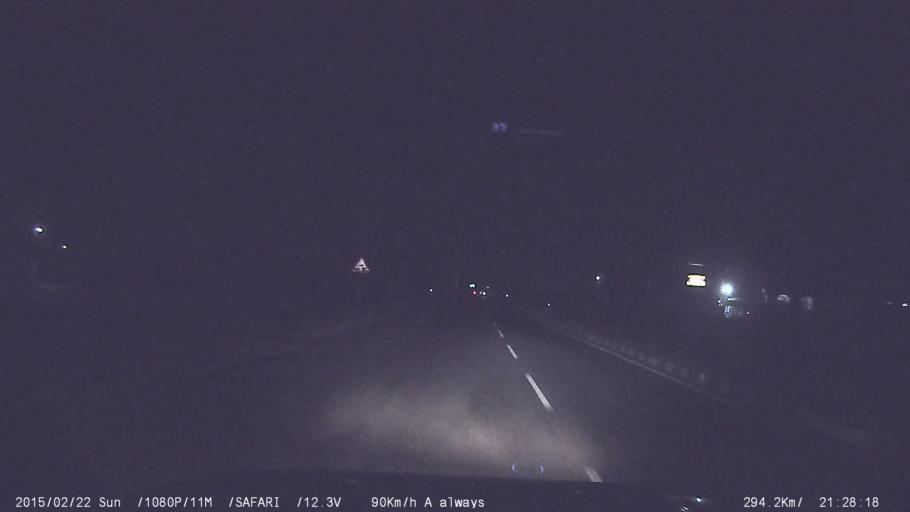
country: IN
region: Tamil Nadu
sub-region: Karur
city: Karur
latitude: 10.9242
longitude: 78.0476
